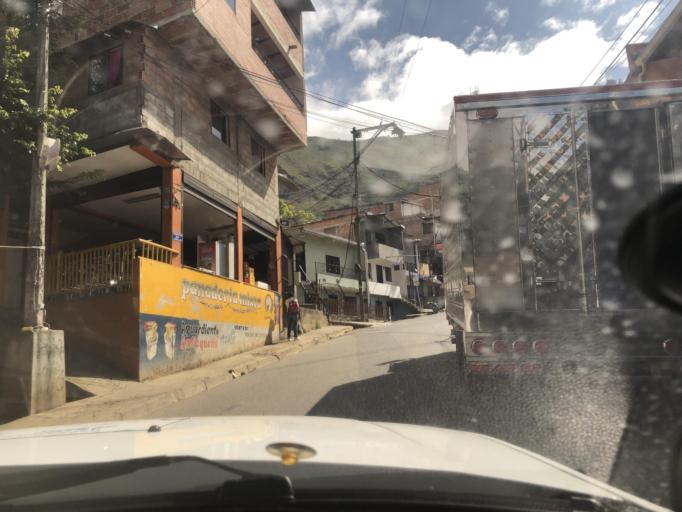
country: CO
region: Antioquia
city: Bello
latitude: 6.3093
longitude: -75.5472
